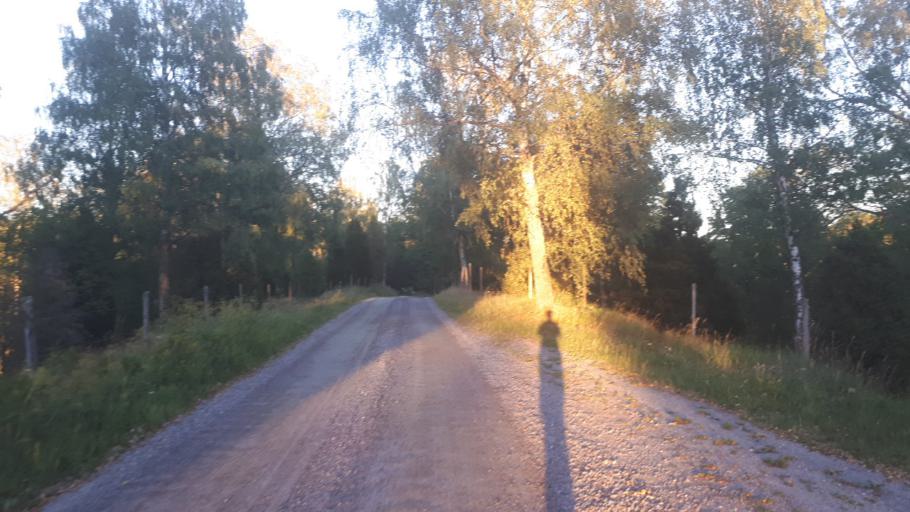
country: SE
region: Soedermanland
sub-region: Flens Kommun
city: Halleforsnas
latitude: 59.0736
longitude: 16.3765
